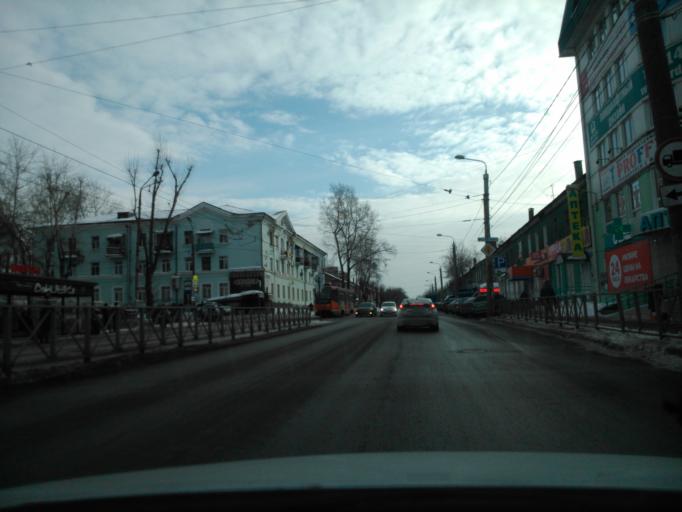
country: RU
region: Perm
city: Perm
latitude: 57.9984
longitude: 56.2427
